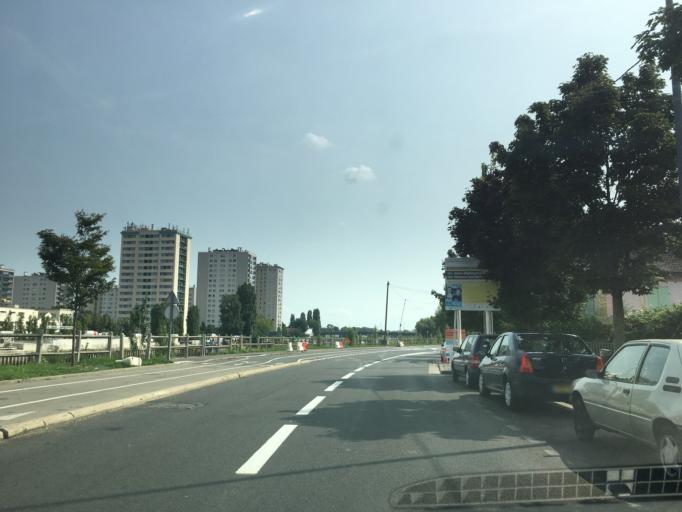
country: FR
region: Ile-de-France
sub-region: Departement du Val-de-Marne
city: Creteil
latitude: 48.8040
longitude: 2.4677
